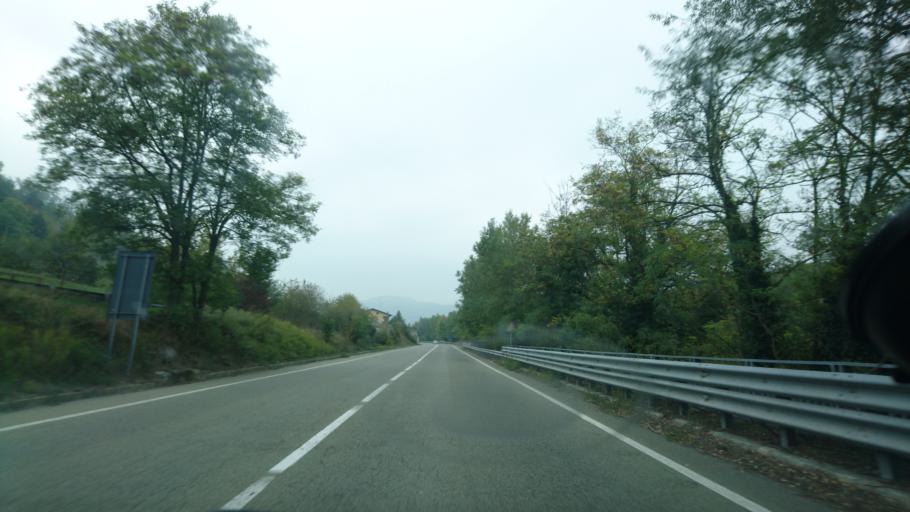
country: IT
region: Piedmont
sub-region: Provincia di Alessandria
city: Ponti
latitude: 44.6294
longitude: 8.3611
